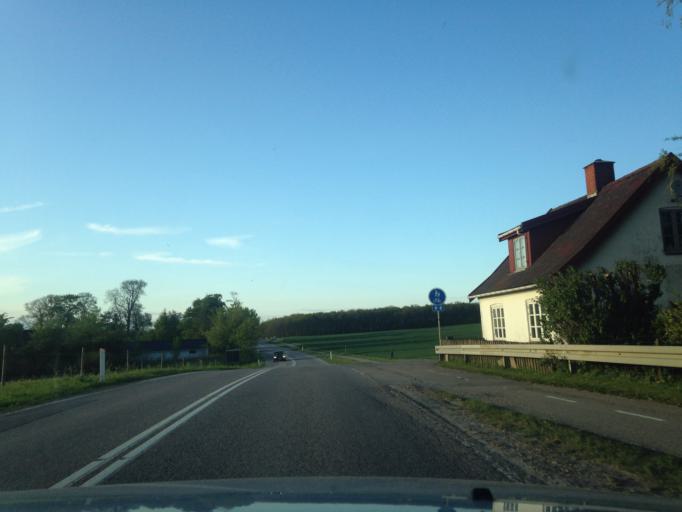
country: DK
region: Capital Region
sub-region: Hoje-Taastrup Kommune
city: Flong
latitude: 55.6334
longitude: 12.1929
